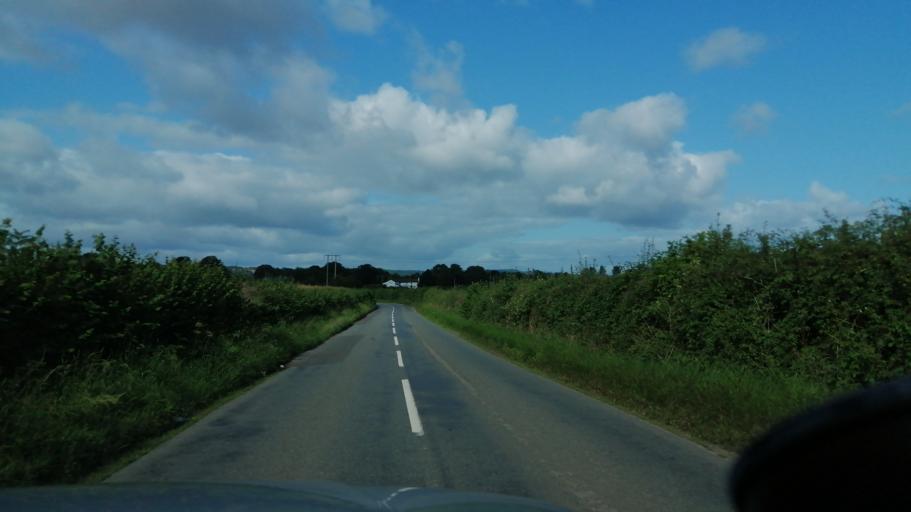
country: GB
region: England
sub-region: Herefordshire
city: Madley
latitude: 52.0403
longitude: -2.8328
